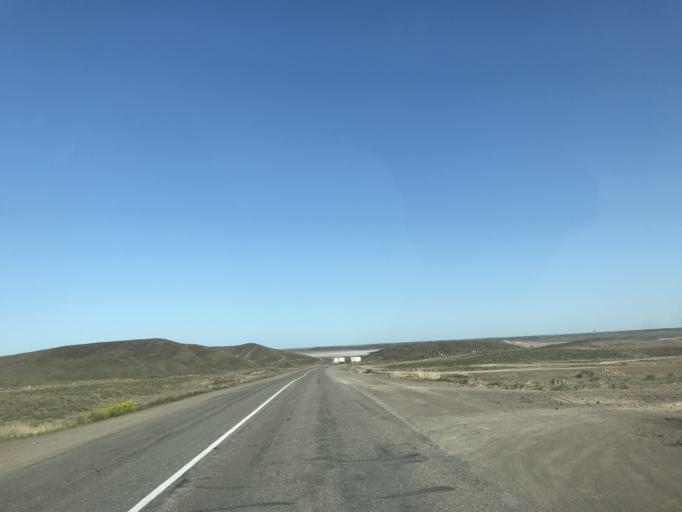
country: KZ
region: Zhambyl
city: Mynaral
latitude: 45.3257
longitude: 73.7355
